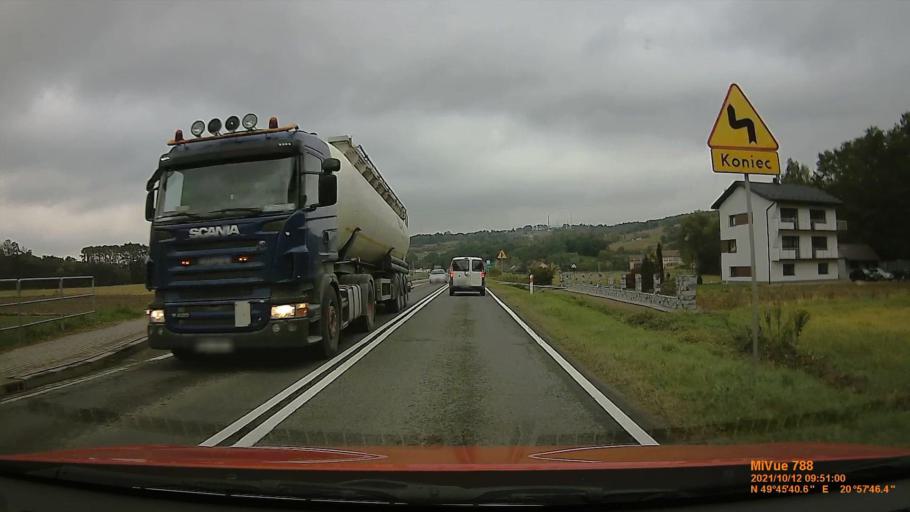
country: PL
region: Lesser Poland Voivodeship
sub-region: Powiat tarnowski
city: Ciezkowice
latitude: 49.7614
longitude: 20.9630
